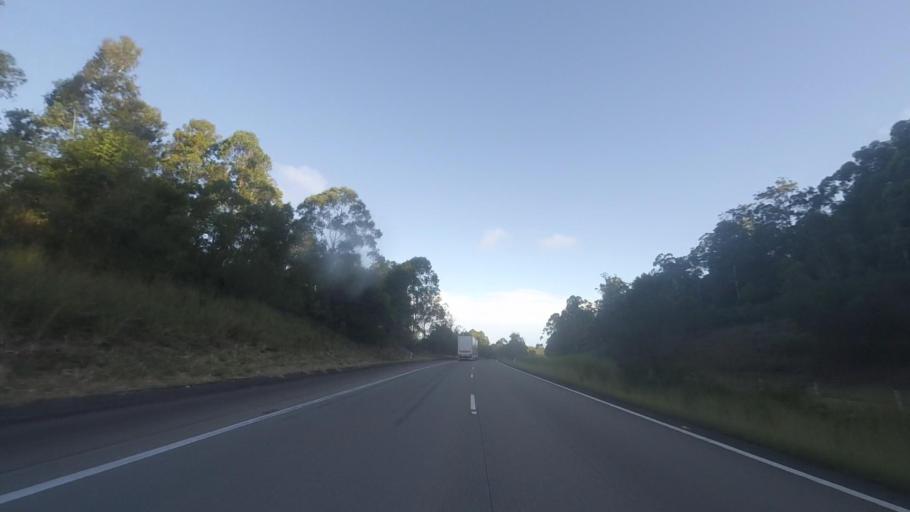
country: AU
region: New South Wales
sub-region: Great Lakes
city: Bulahdelah
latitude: -32.2849
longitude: 152.3393
